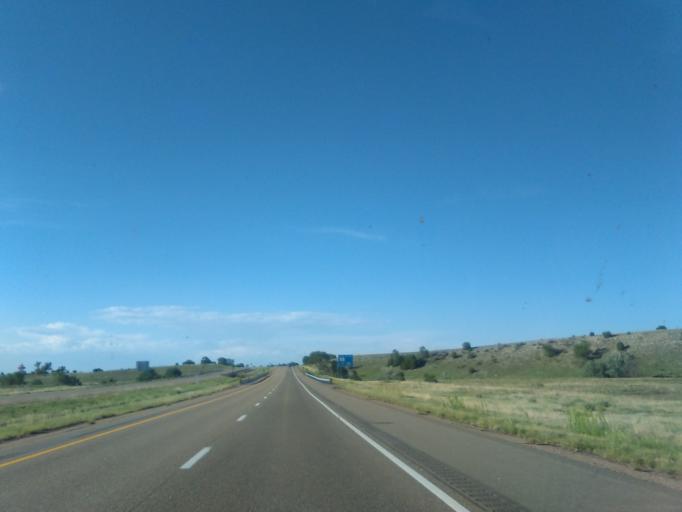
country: US
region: New Mexico
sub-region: San Miguel County
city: Las Vegas
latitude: 35.6081
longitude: -105.2052
